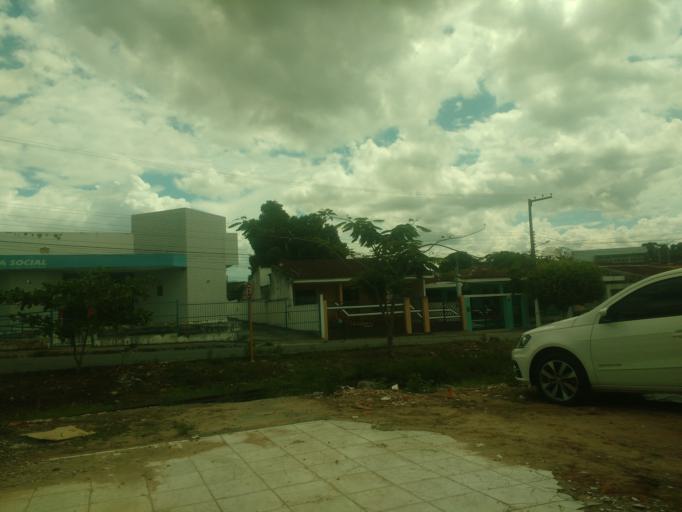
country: BR
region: Alagoas
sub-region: Uniao Dos Palmares
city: Uniao dos Palmares
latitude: -9.1611
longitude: -36.0312
